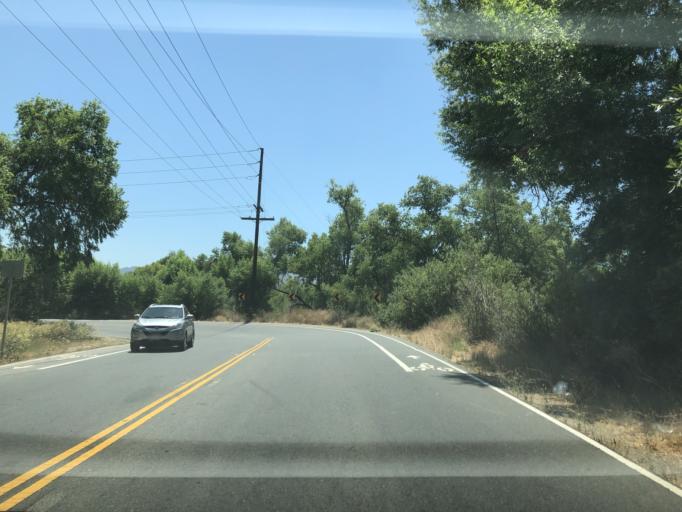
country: US
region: California
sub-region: Riverside County
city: Corona
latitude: 33.9049
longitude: -117.5998
